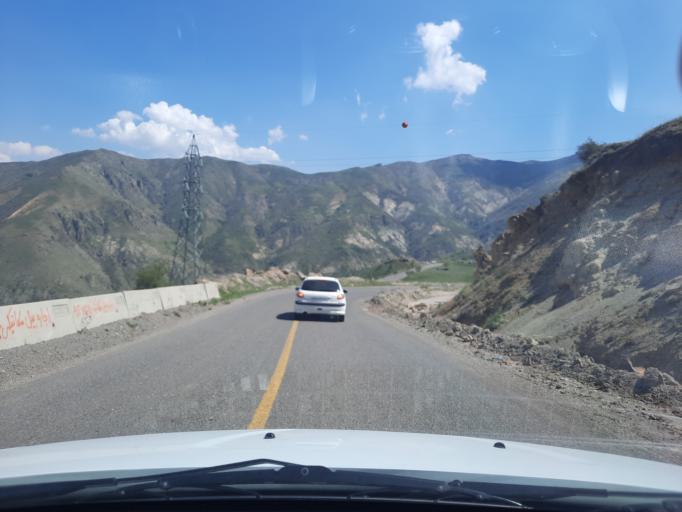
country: IR
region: Qazvin
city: Qazvin
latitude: 36.4115
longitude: 50.2440
